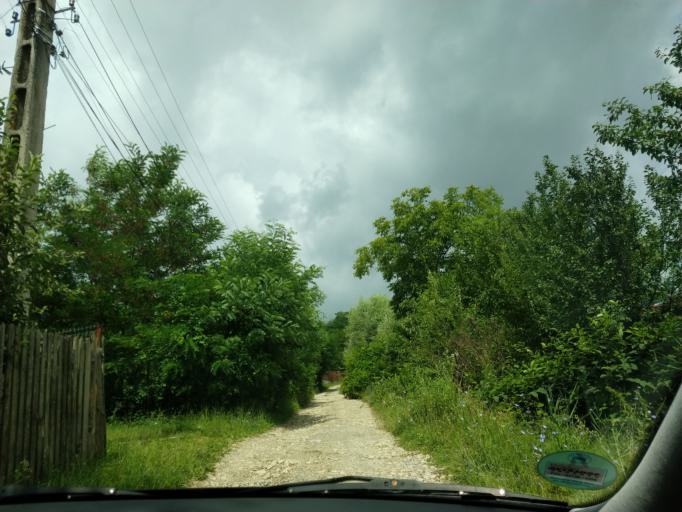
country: RO
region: Prahova
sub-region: Oras Breaza
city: Valea Tarsei
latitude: 45.1857
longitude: 25.6272
